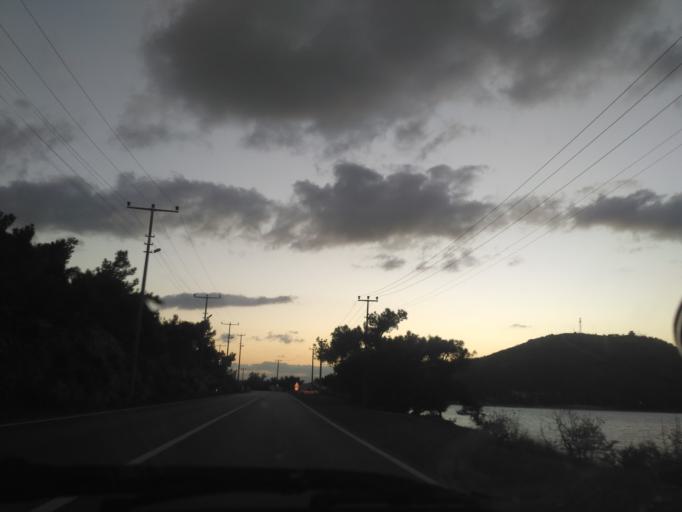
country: TR
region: Balikesir
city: Ayvalik
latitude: 39.2810
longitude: 26.6729
